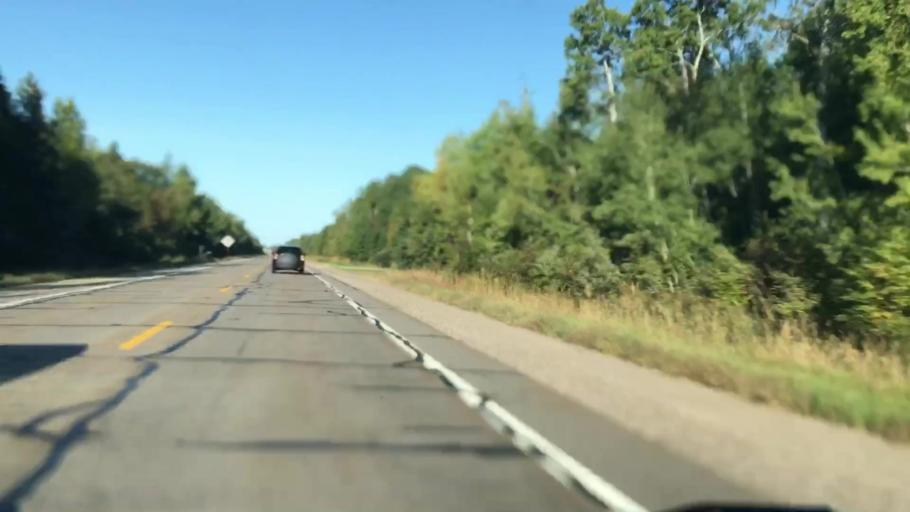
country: US
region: Michigan
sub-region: Chippewa County
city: Sault Ste. Marie
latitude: 46.3758
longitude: -84.6264
